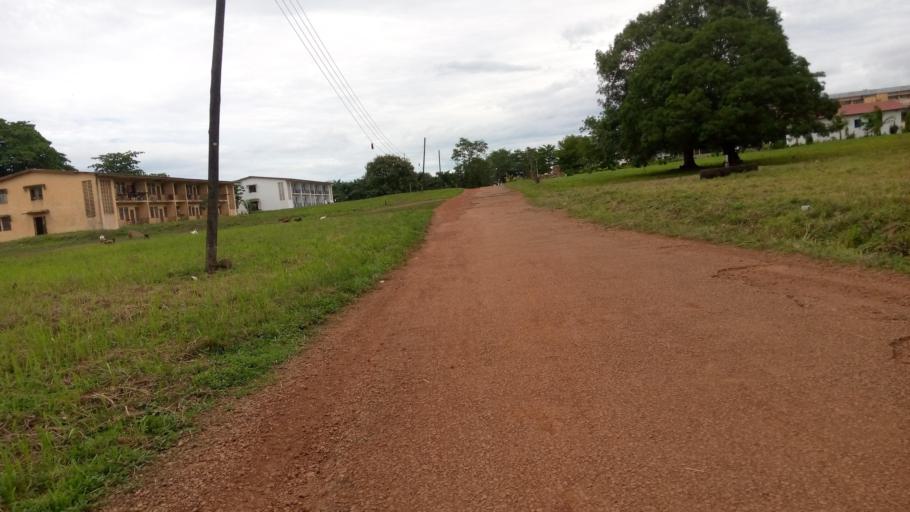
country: SL
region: Southern Province
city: Largo
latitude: 8.1179
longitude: -12.0709
